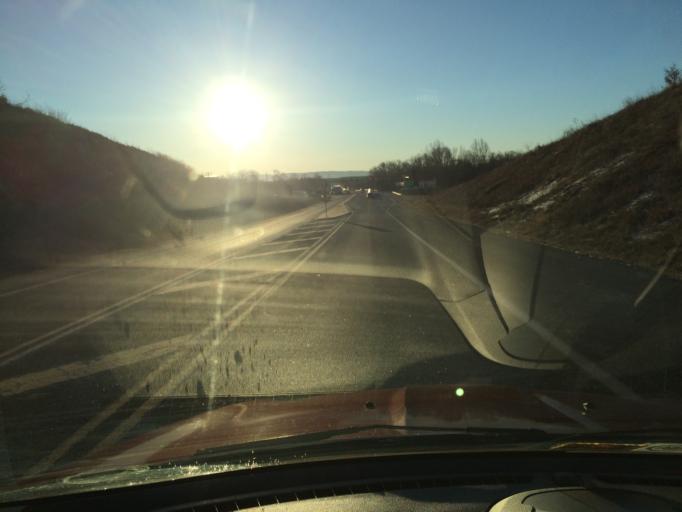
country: US
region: Virginia
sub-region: Augusta County
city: Verona
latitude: 38.1828
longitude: -79.0345
